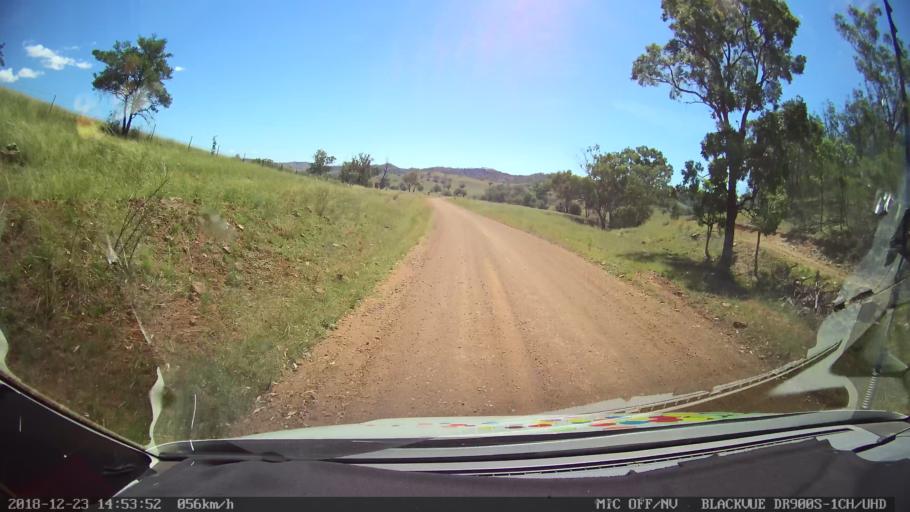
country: AU
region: New South Wales
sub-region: Tamworth Municipality
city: Manilla
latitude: -30.6931
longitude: 150.8504
